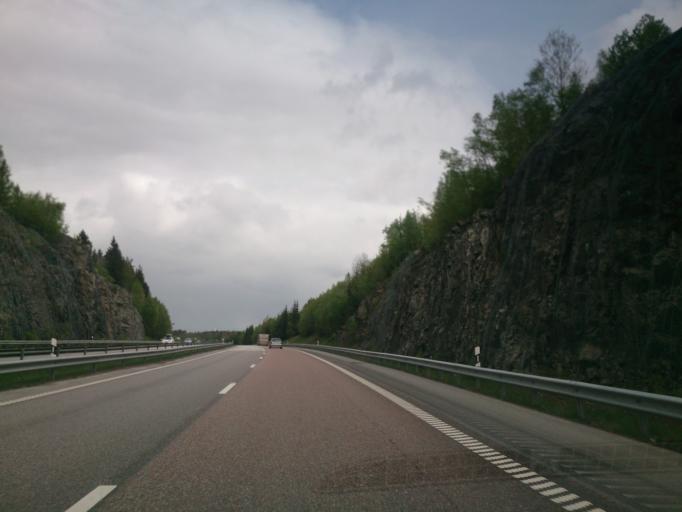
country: SE
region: Stockholm
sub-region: Sodertalje Kommun
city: Pershagen
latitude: 59.1334
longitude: 17.6449
